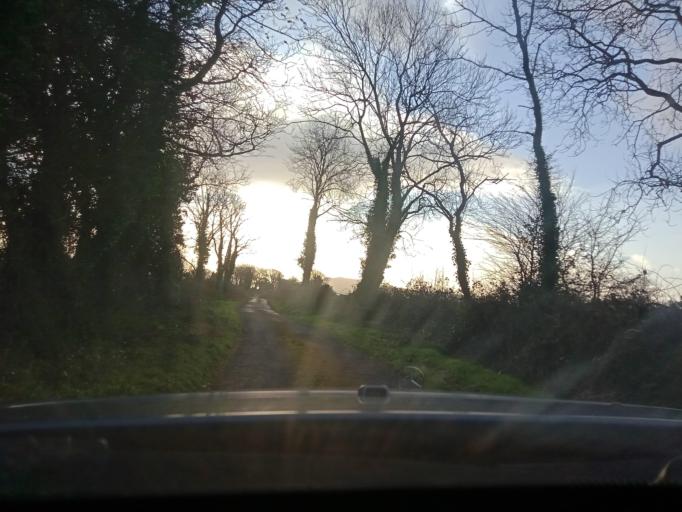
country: IE
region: Leinster
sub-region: Kilkenny
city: Callan
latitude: 52.4525
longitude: -7.4201
